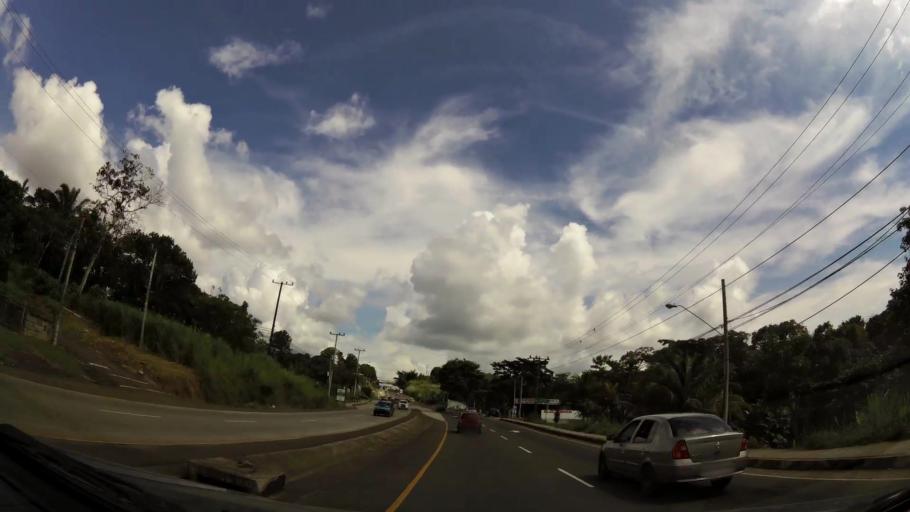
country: PA
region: Panama
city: Vista Alegre
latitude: 8.9362
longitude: -79.6854
